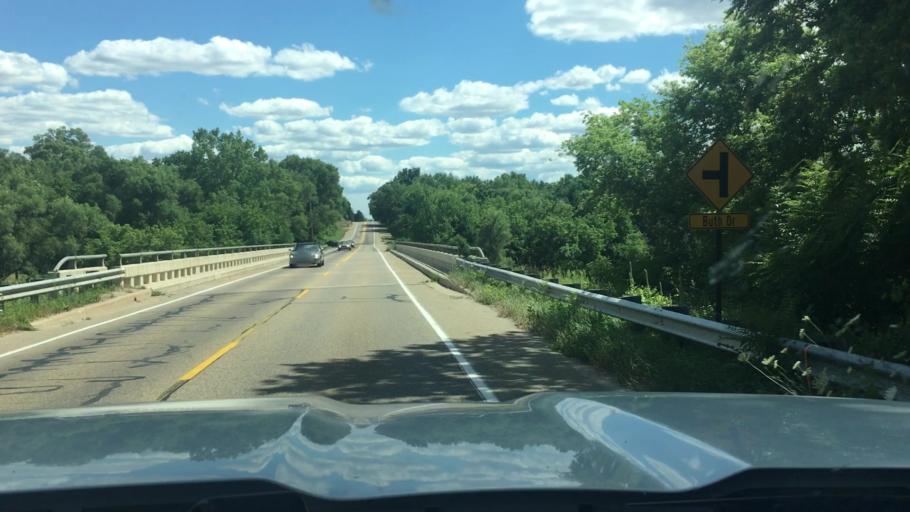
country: US
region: Michigan
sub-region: Kent County
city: Comstock Park
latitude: 43.0698
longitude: -85.6540
